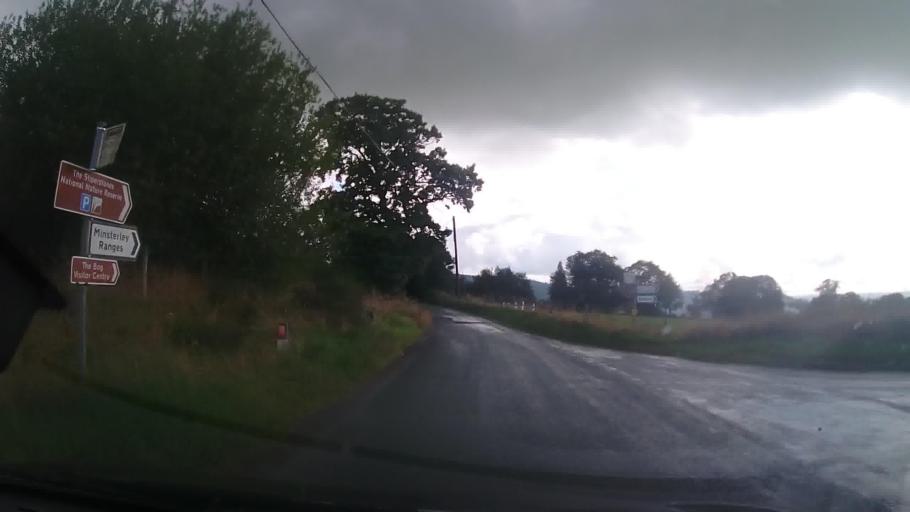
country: GB
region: England
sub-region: Shropshire
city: Norbury
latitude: 52.5830
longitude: -2.9558
